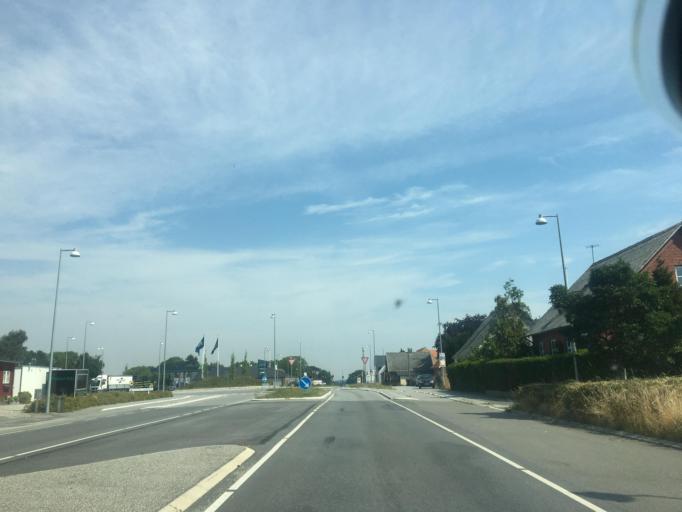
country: DK
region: Zealand
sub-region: Faxe Kommune
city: Ronnede
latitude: 55.2568
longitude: 12.0201
